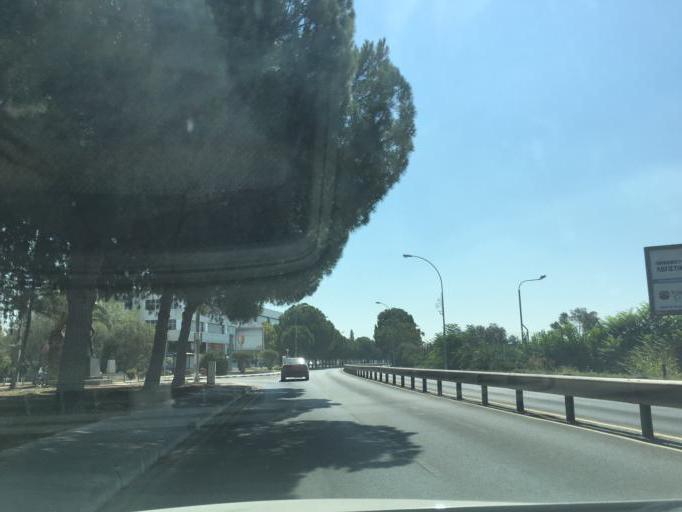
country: CY
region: Lefkosia
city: Nicosia
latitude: 35.1638
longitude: 33.3329
